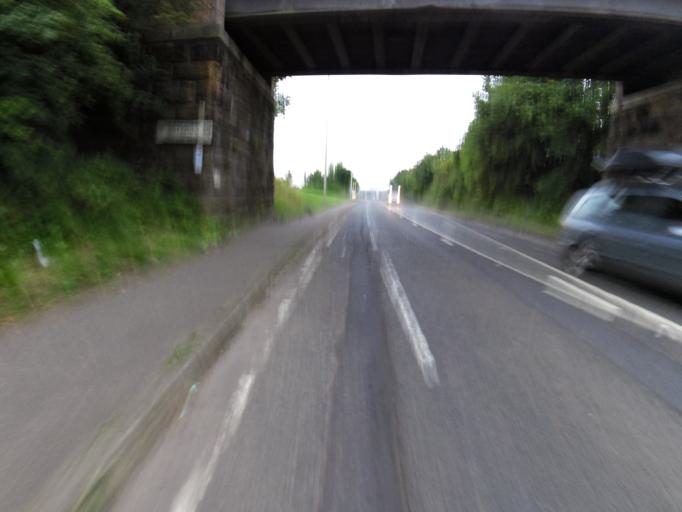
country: GB
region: Scotland
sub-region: Midlothian
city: Bonnyrigg
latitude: 55.9083
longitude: -3.1063
